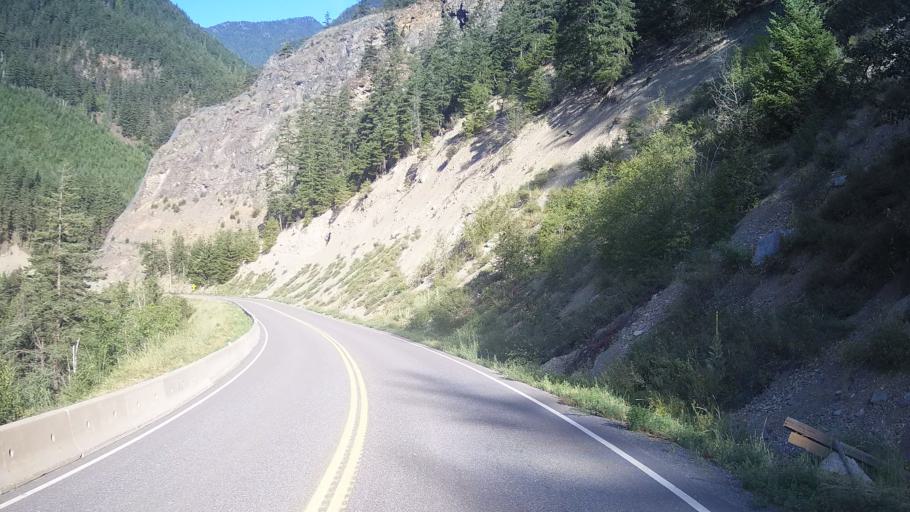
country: CA
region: British Columbia
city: Lillooet
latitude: 50.6425
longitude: -122.0468
